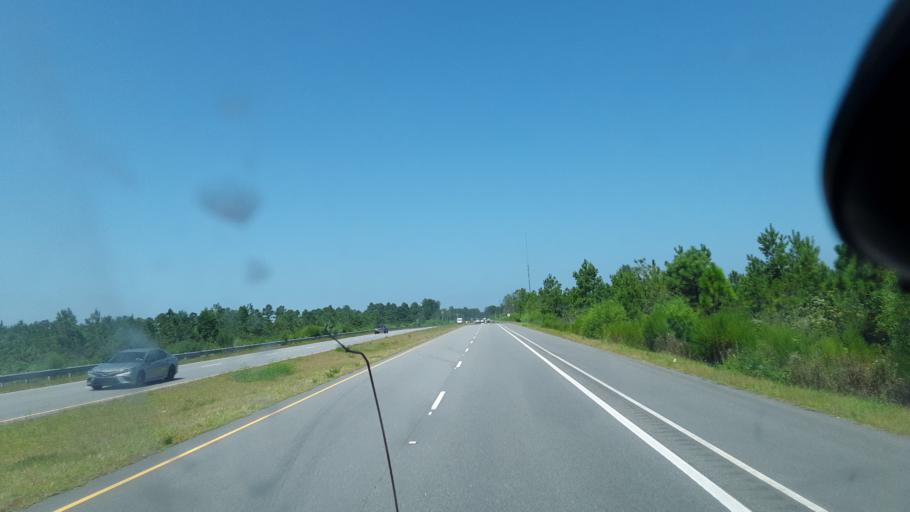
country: US
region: South Carolina
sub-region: Horry County
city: Forestbrook
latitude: 33.8104
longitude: -78.8975
